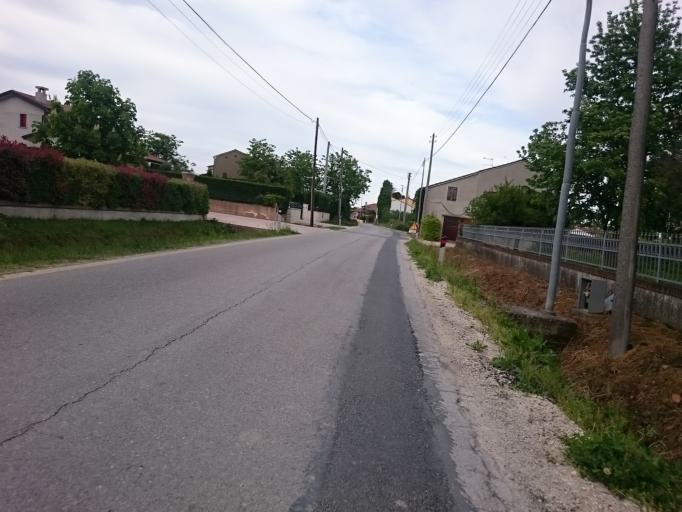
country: IT
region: Veneto
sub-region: Provincia di Padova
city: Sant'Elena
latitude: 45.1734
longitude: 11.7239
